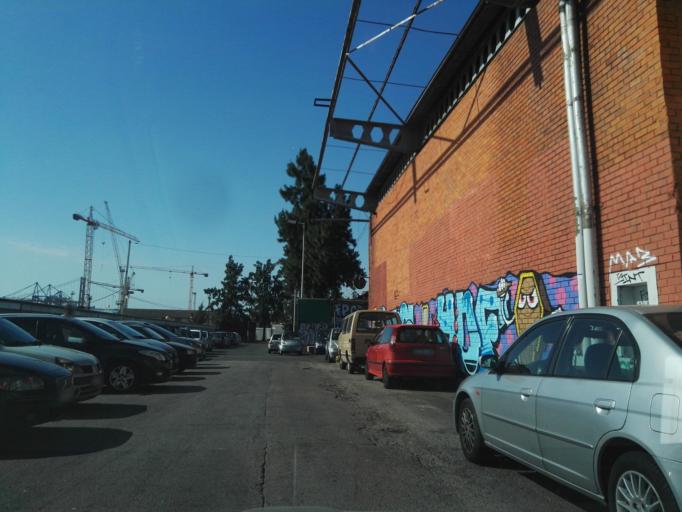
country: PT
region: Setubal
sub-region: Almada
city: Cacilhas
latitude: 38.7047
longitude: -9.1559
